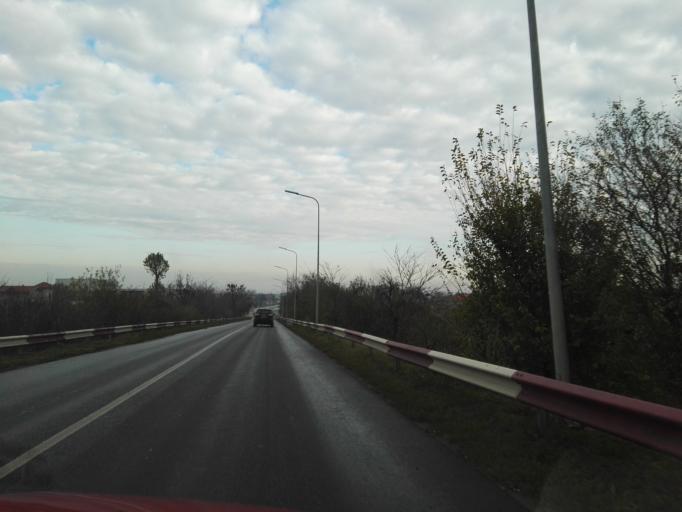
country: RO
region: Ilfov
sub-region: Comuna Magurele
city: Magurele
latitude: 44.3595
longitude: 26.0374
